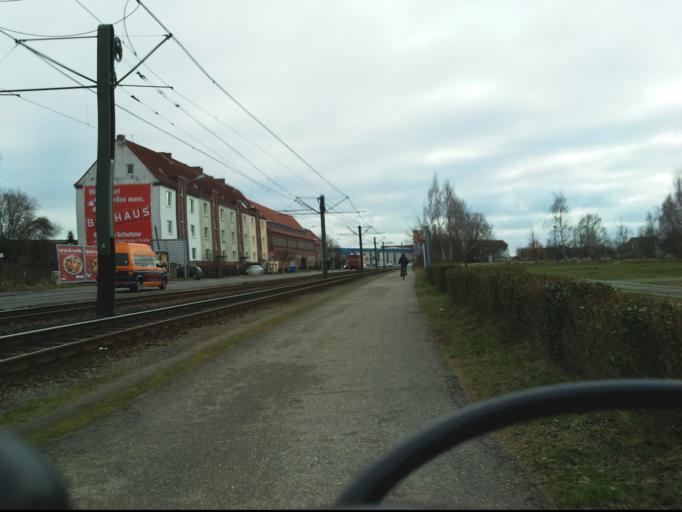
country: DE
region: Mecklenburg-Vorpommern
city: Dierkow-West
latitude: 54.0956
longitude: 12.1577
